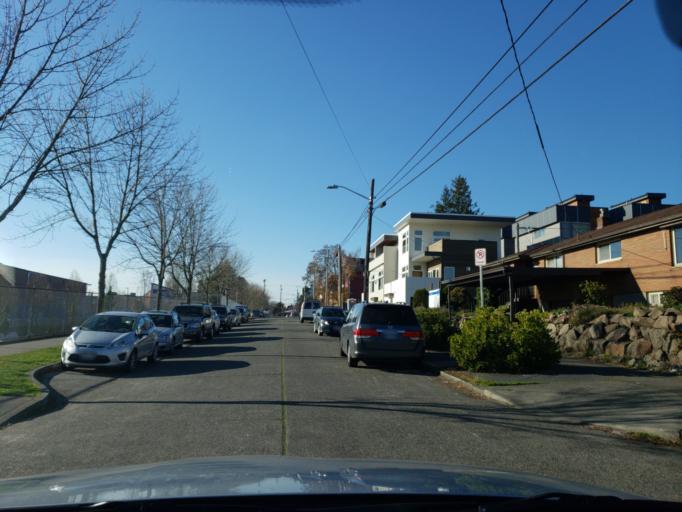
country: US
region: Washington
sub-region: King County
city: Seattle
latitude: 47.6778
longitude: -122.3730
